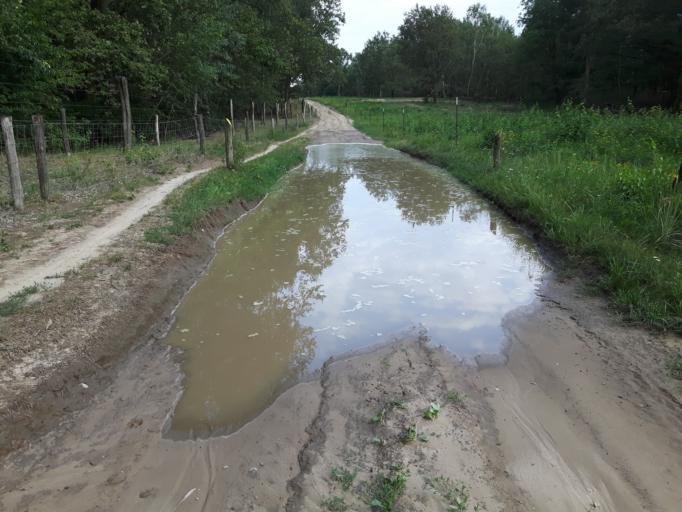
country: DE
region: Brandenburg
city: Dallgow-Doeberitz
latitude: 52.4836
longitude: 13.0288
